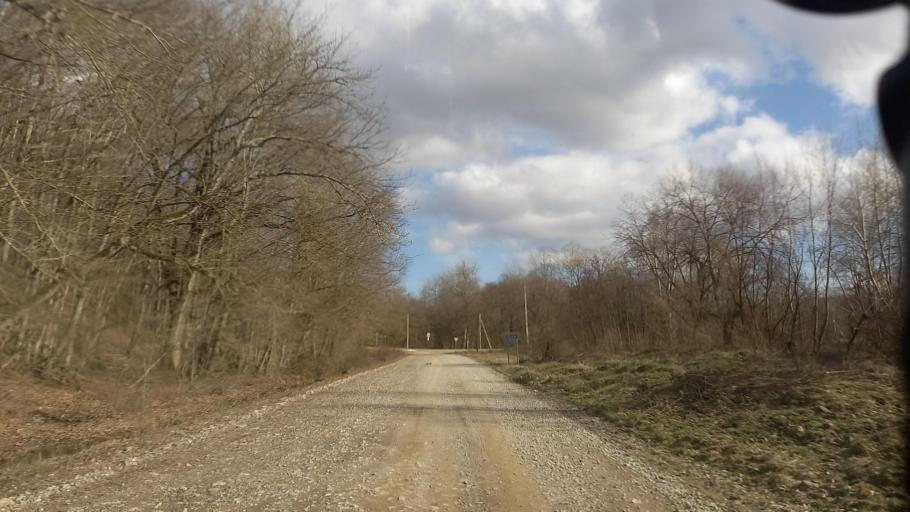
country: RU
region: Krasnodarskiy
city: Smolenskaya
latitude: 44.6054
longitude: 38.8405
